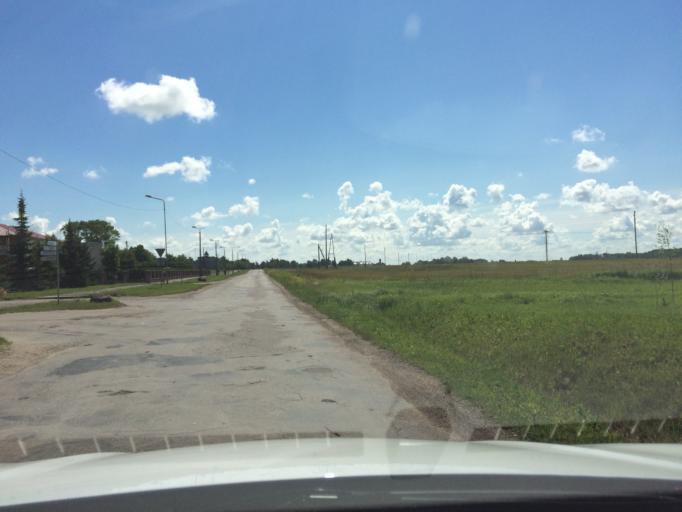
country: LV
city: Tervete
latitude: 56.5260
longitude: 23.5091
